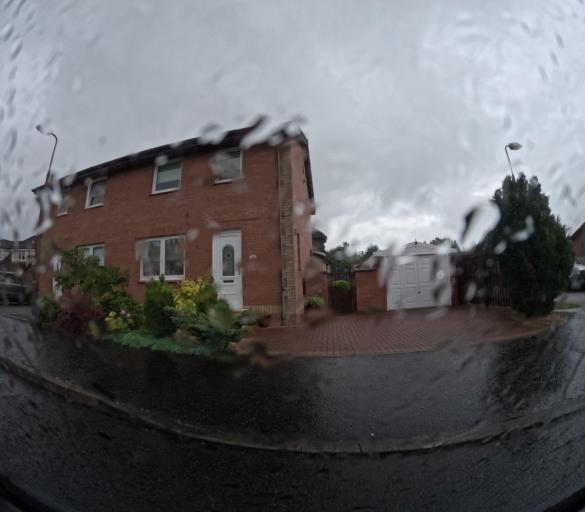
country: GB
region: Scotland
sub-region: West Lothian
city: West Calder
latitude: 55.8804
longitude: -3.5870
